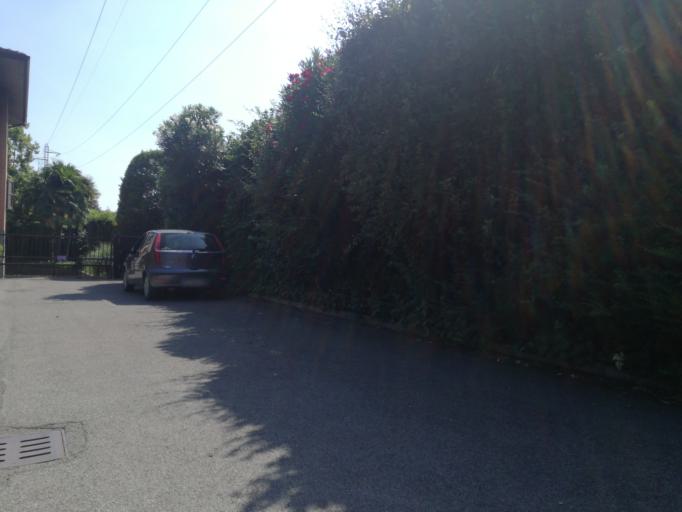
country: IT
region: Lombardy
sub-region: Provincia di Bergamo
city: Calusco d'Adda
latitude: 45.6861
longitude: 9.4733
